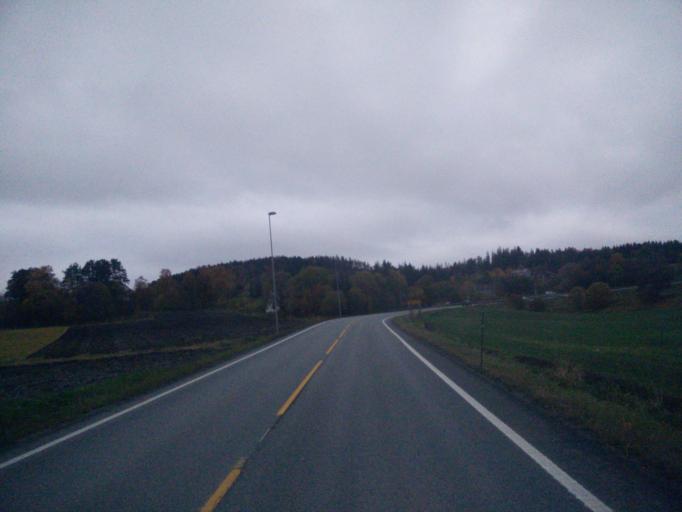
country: NO
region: Nord-Trondelag
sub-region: Stjordal
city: Stjordal
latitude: 63.5077
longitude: 10.8543
